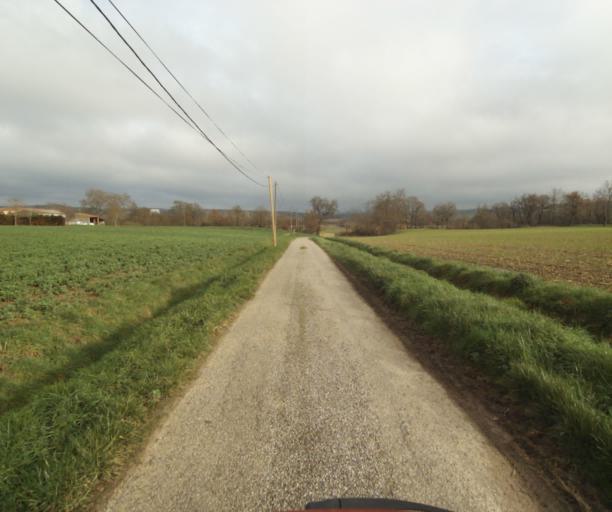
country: FR
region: Languedoc-Roussillon
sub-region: Departement de l'Aude
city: Belpech
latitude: 43.1905
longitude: 1.7272
